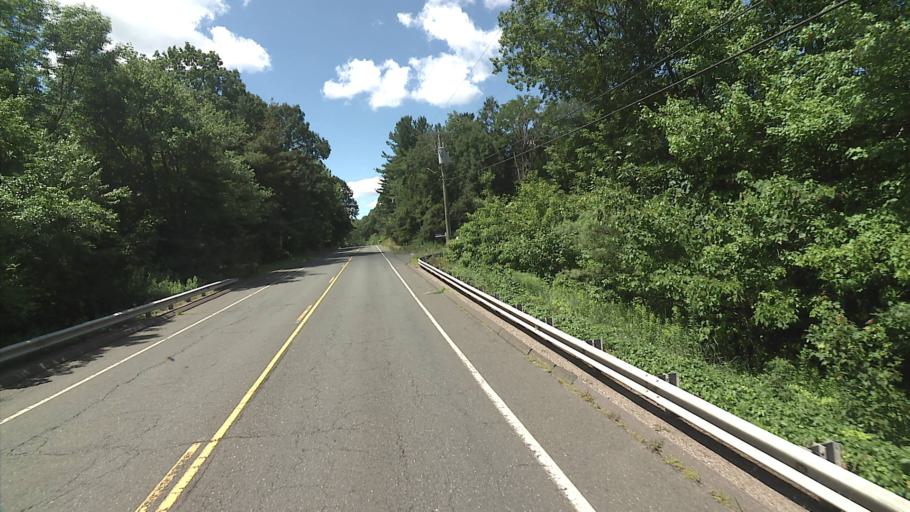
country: US
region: Connecticut
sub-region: Hartford County
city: North Granby
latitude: 41.9476
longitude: -72.8986
